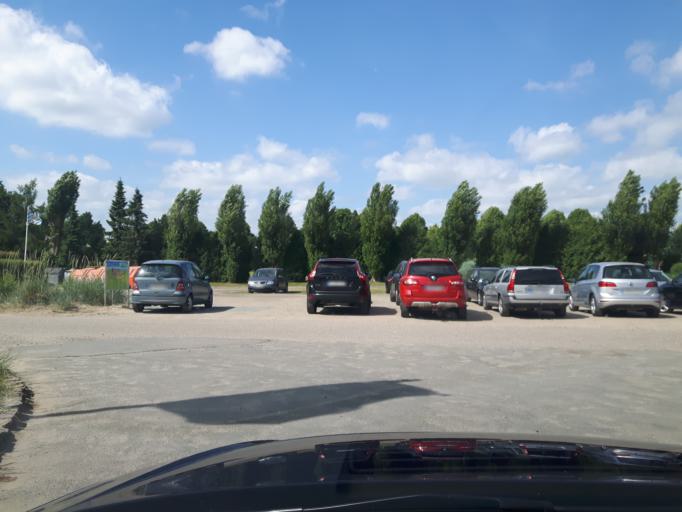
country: DE
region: Schleswig-Holstein
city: Neustadt in Holstein
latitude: 54.0902
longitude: 10.8363
